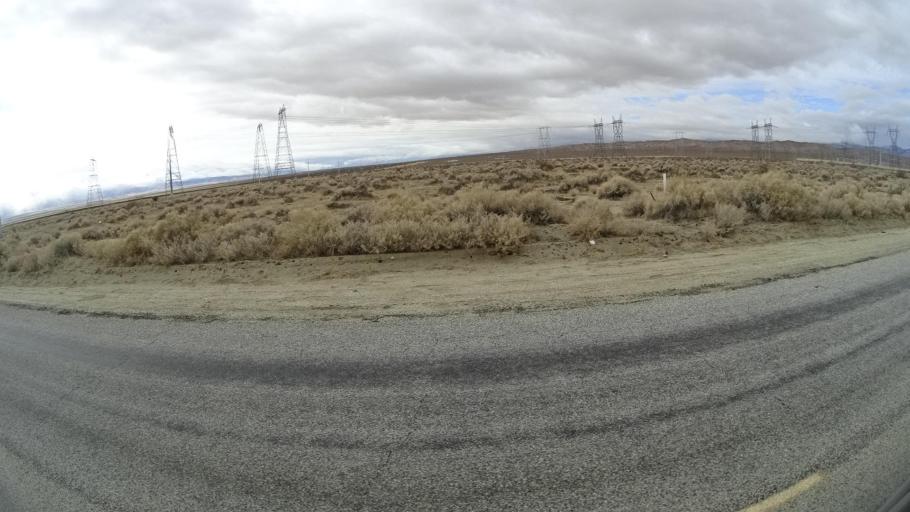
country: US
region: California
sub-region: Los Angeles County
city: Green Valley
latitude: 34.8500
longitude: -118.4319
